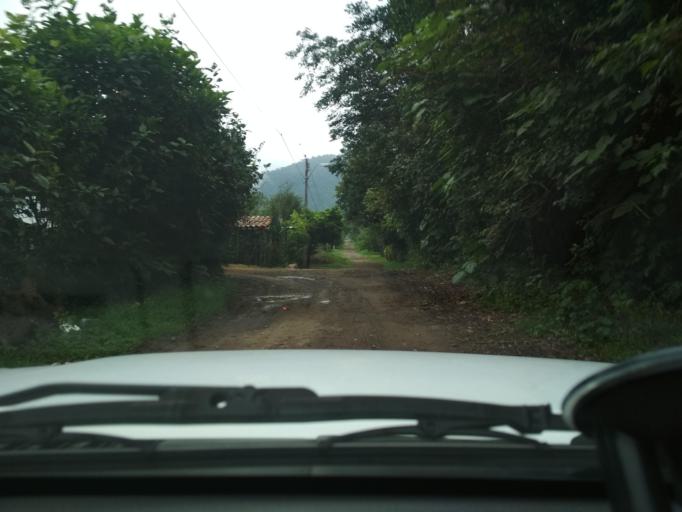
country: MX
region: Veracruz
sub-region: Ixtaczoquitlan
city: Buenavista
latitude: 18.9140
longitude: -97.0505
